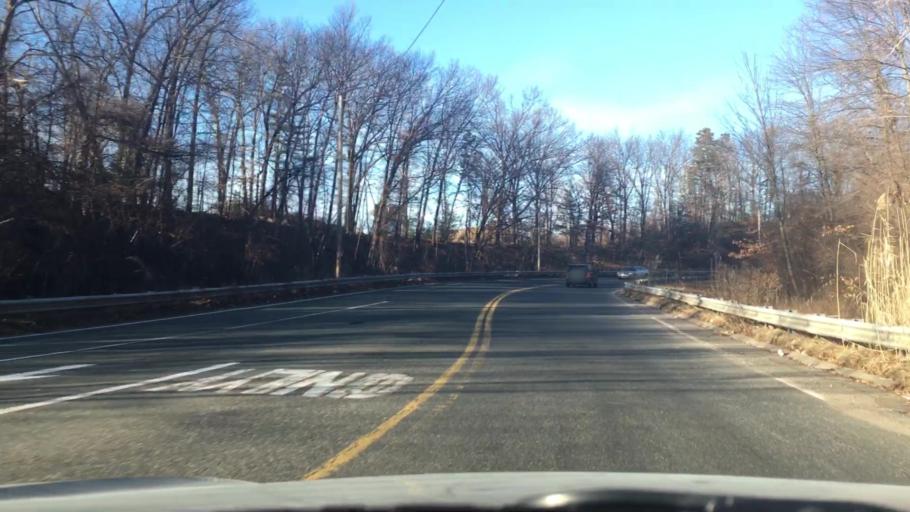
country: US
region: Massachusetts
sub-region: Hampden County
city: North Chicopee
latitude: 42.1595
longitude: -72.5494
